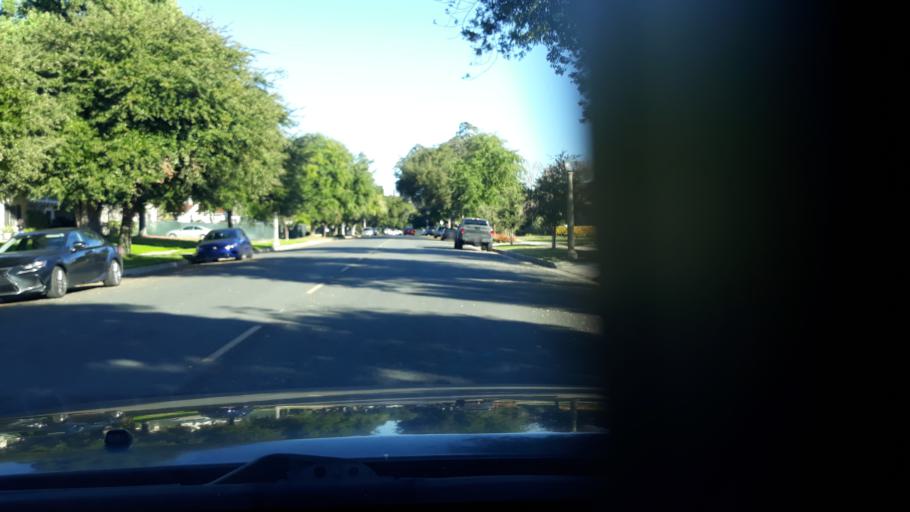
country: US
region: California
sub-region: Los Angeles County
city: San Marino
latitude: 34.1151
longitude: -118.1075
